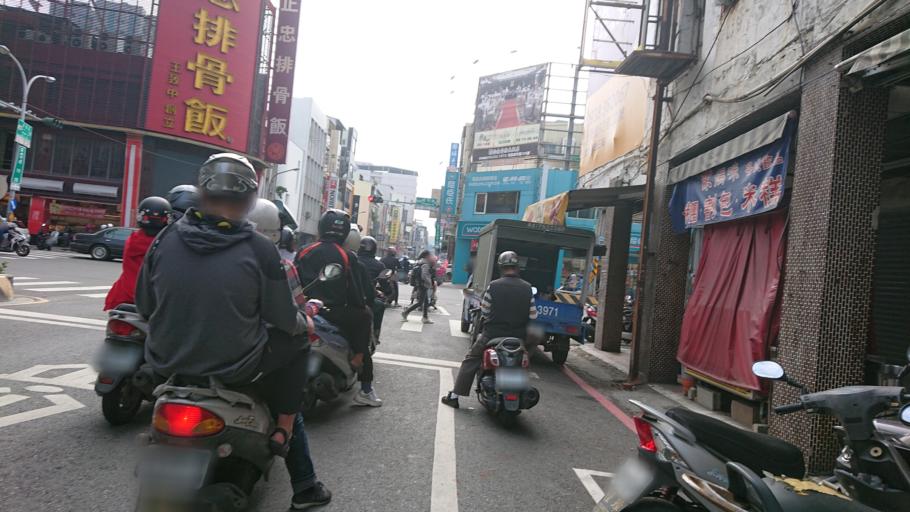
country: TW
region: Taiwan
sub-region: Tainan
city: Tainan
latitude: 22.9987
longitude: 120.2050
